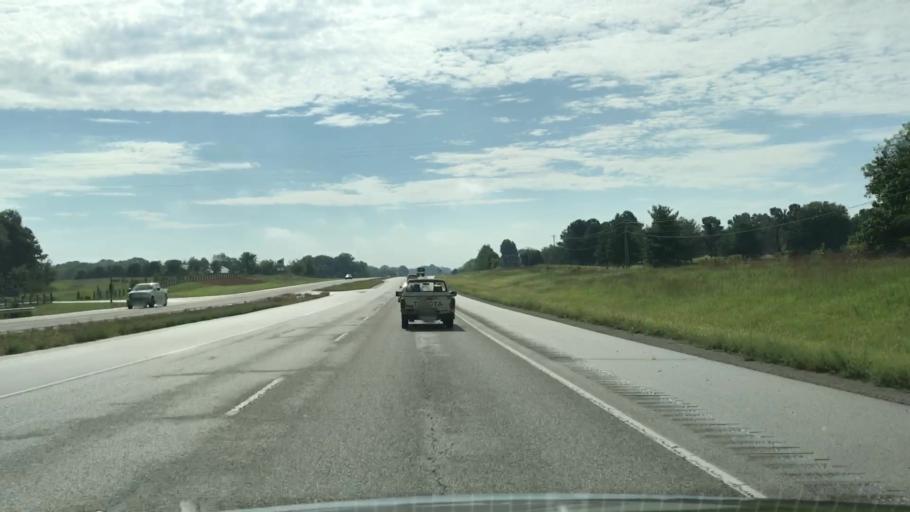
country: US
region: Kentucky
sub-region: Warren County
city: Plano
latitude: 36.8883
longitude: -86.3702
